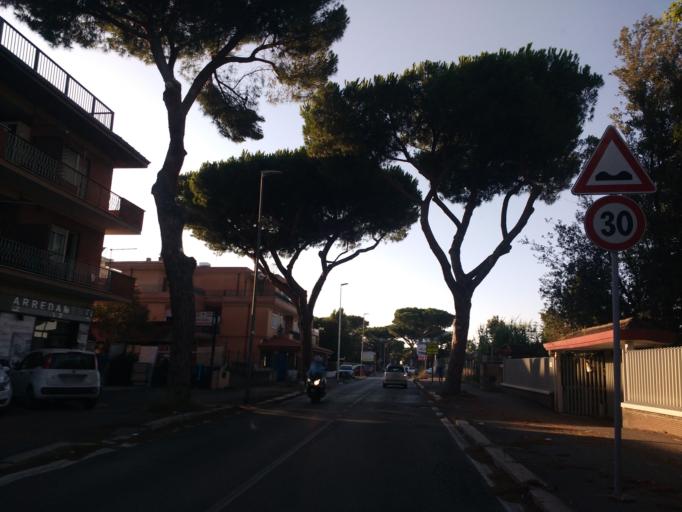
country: IT
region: Latium
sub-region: Citta metropolitana di Roma Capitale
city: Acilia-Castel Fusano-Ostia Antica
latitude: 41.7779
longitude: 12.3685
